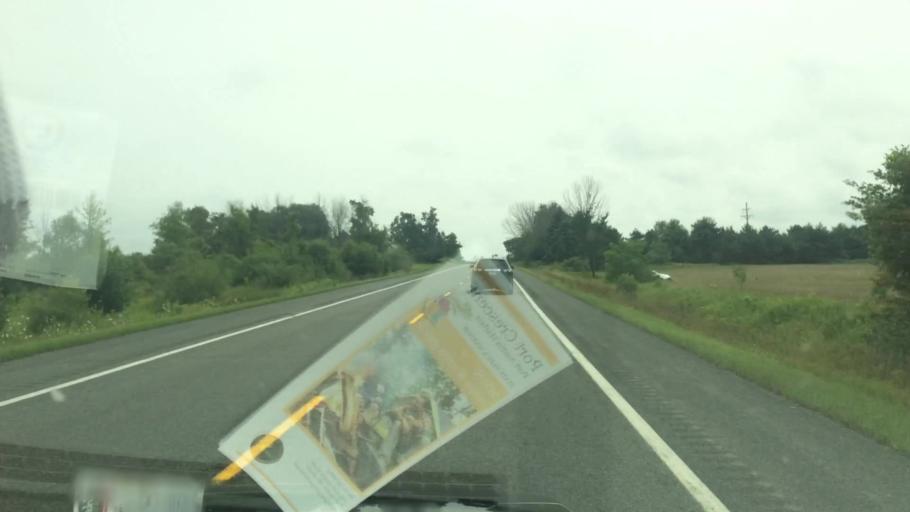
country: US
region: Michigan
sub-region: Huron County
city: Harbor Beach
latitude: 44.0126
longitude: -82.7953
